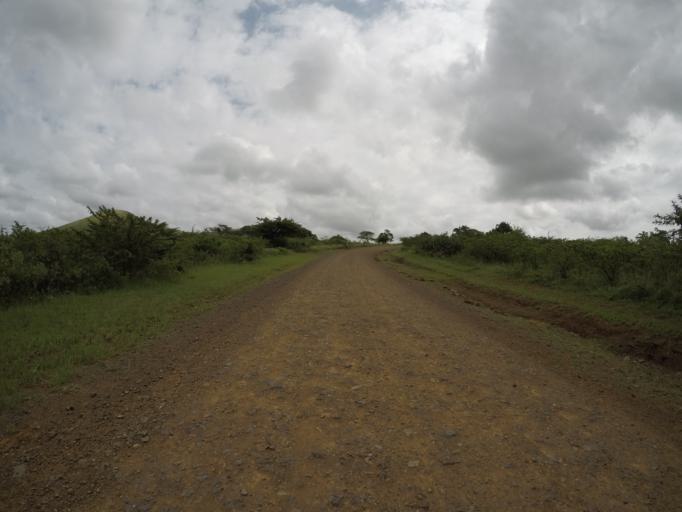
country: ZA
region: KwaZulu-Natal
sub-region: uThungulu District Municipality
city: Empangeni
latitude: -28.5946
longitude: 31.8908
